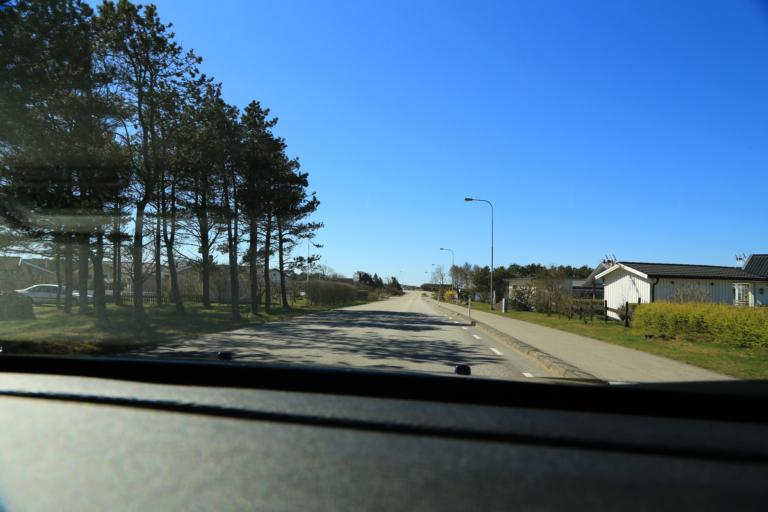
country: SE
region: Halland
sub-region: Varbergs Kommun
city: Traslovslage
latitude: 57.0663
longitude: 12.2817
